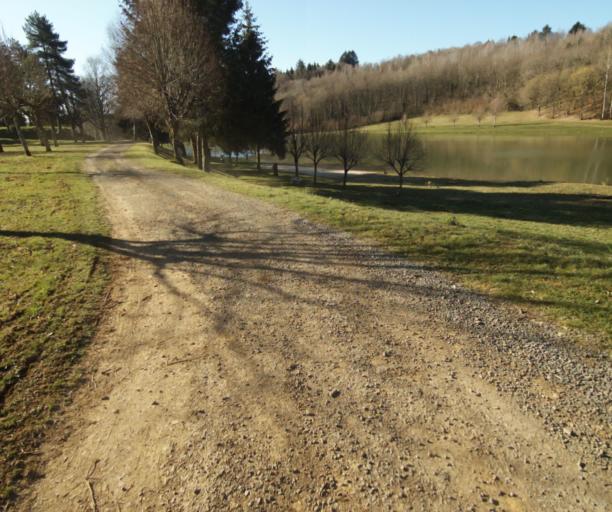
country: FR
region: Limousin
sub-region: Departement de la Correze
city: Seilhac
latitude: 45.3938
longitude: 1.7581
